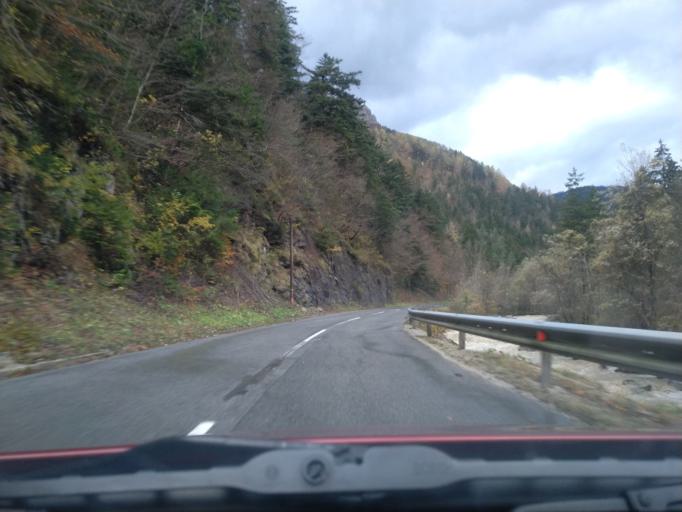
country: SI
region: Luce
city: Luce
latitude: 46.3843
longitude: 14.7229
